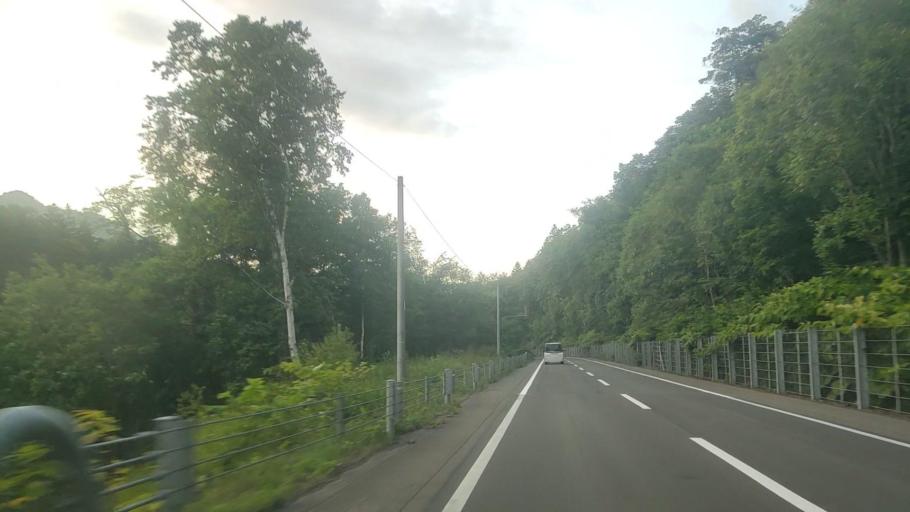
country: JP
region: Hokkaido
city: Ashibetsu
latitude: 43.3402
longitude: 142.1533
